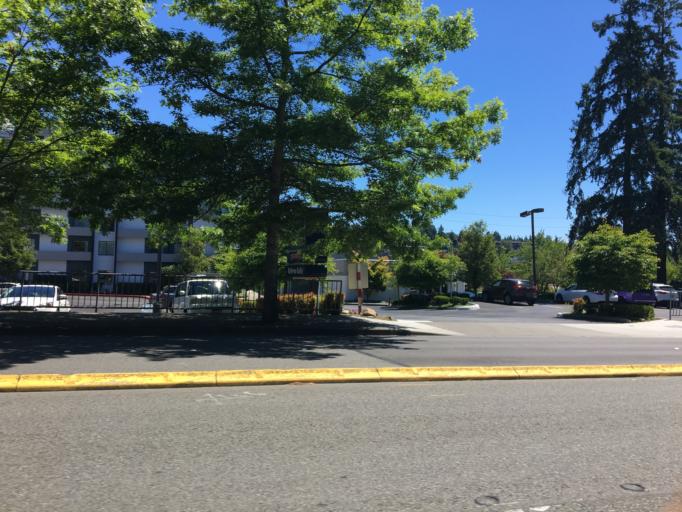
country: US
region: Washington
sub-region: King County
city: Bellevue
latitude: 47.6109
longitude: -122.1909
